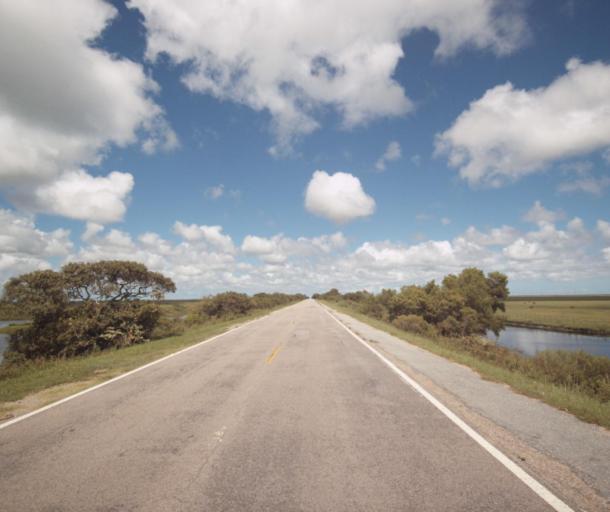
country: BR
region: Rio Grande do Sul
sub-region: Arroio Grande
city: Arroio Grande
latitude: -32.5449
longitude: -52.5426
